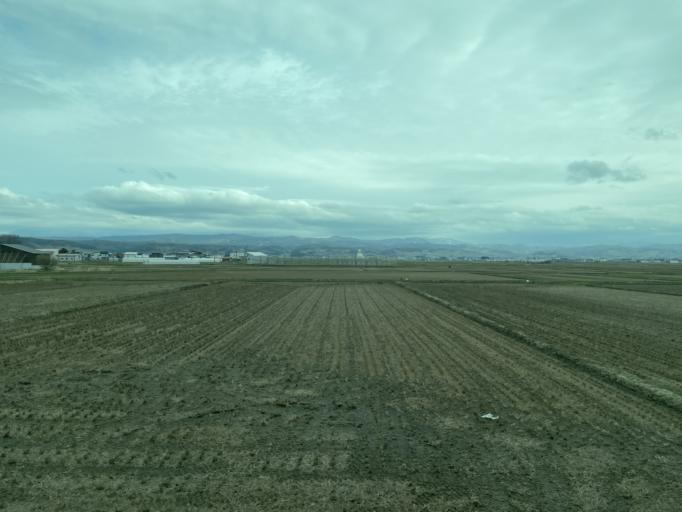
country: JP
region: Aomori
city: Namioka
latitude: 40.7031
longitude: 140.5741
